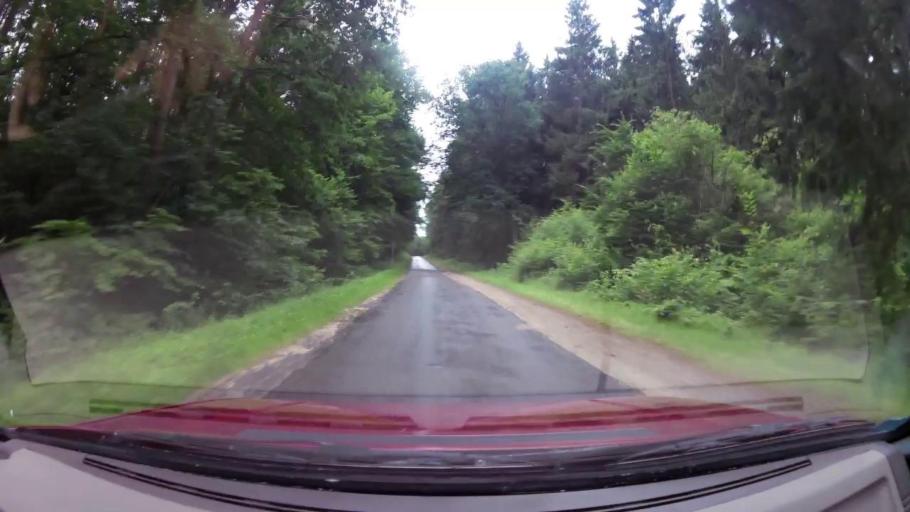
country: PL
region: West Pomeranian Voivodeship
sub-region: Powiat swidwinski
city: Rabino
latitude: 53.9218
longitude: 15.9568
